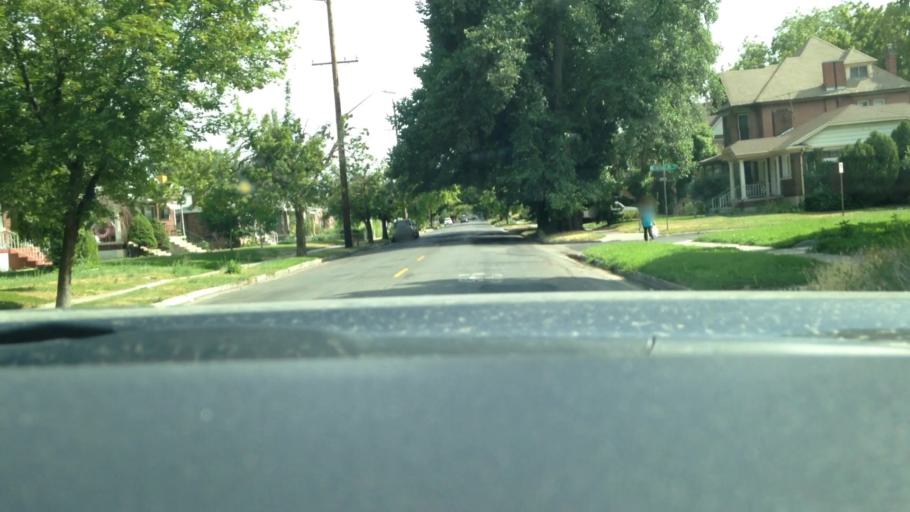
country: US
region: Utah
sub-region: Salt Lake County
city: South Salt Lake
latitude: 40.7319
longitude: -111.8768
